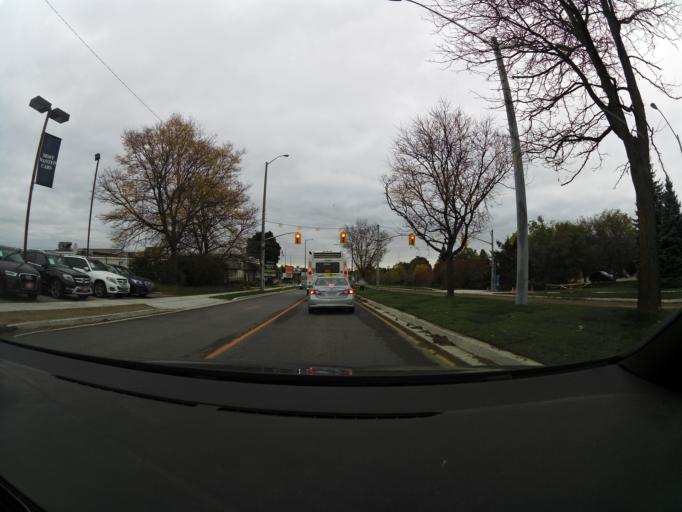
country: CA
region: Ontario
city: Kitchener
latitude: 43.4382
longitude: -80.4623
